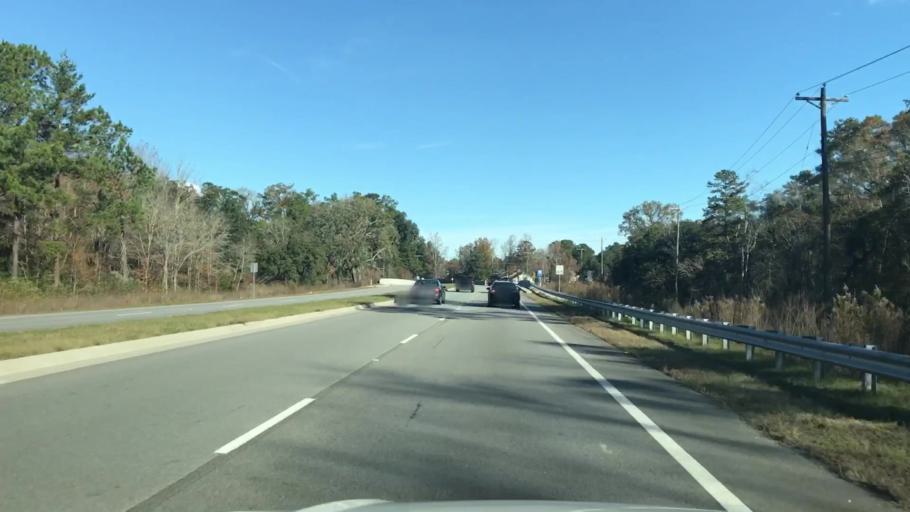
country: US
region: South Carolina
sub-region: Dorchester County
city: Centerville
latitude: 32.9568
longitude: -80.2011
